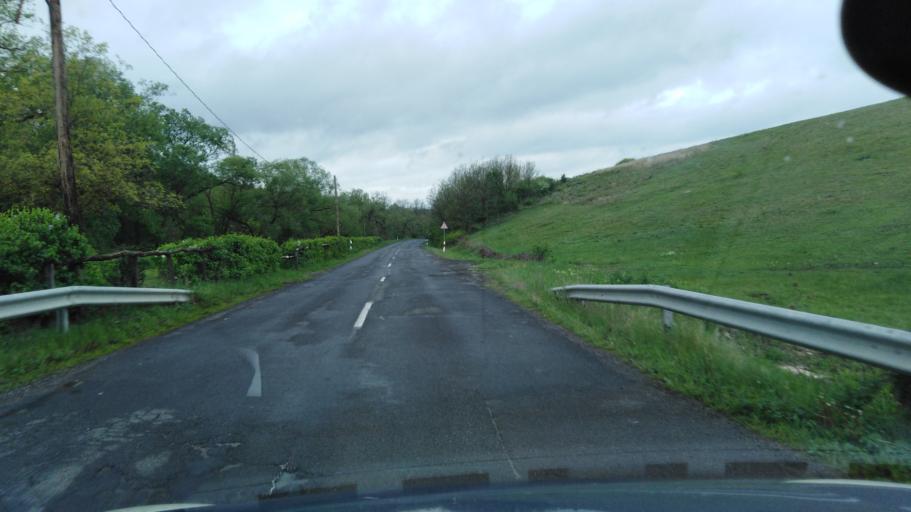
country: HU
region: Nograd
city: Rimoc
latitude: 48.0253
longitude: 19.5858
